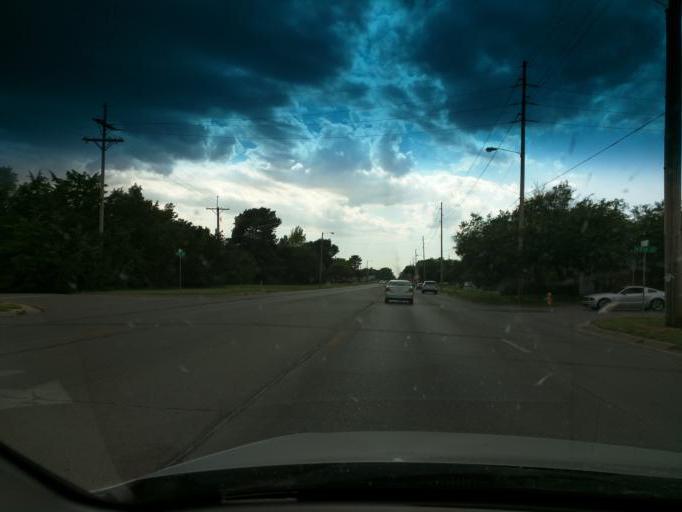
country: US
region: Kansas
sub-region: Reno County
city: Hutchinson
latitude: 38.0867
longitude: -97.9237
